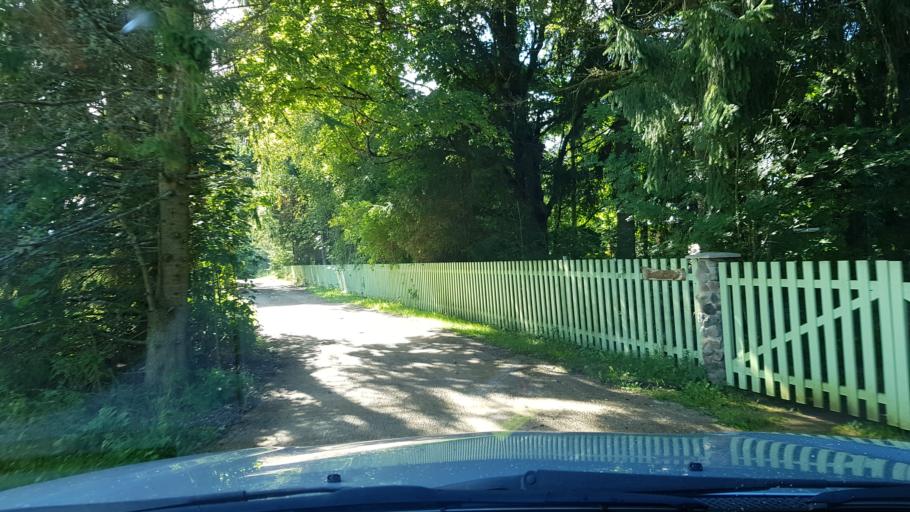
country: EE
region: Harju
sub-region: Raasiku vald
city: Arukula
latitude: 59.2557
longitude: 25.0997
